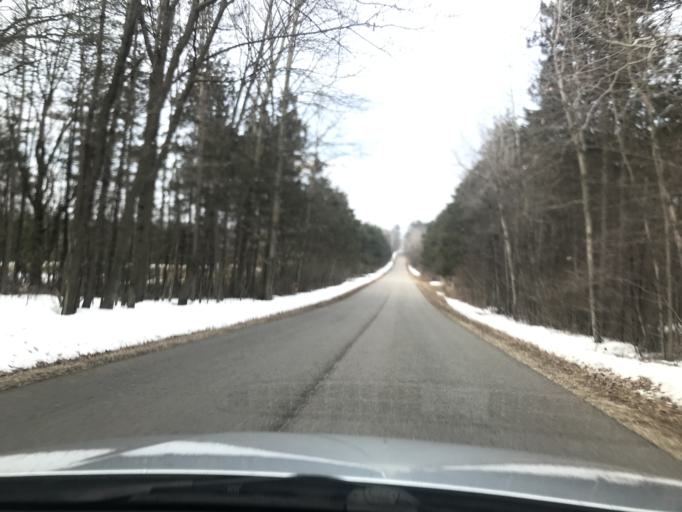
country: US
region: Wisconsin
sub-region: Oconto County
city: Oconto Falls
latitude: 44.8295
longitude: -88.1759
